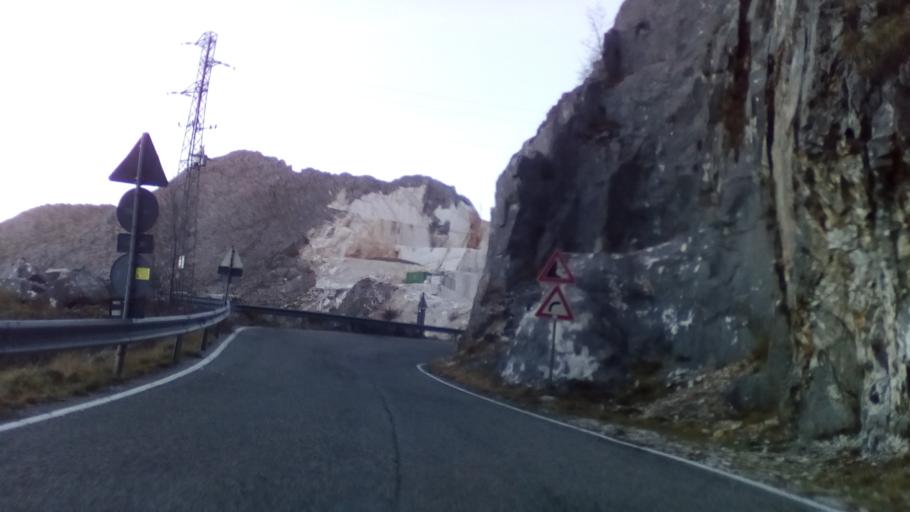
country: IT
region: Tuscany
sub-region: Provincia di Massa-Carrara
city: Montignoso
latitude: 44.0645
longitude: 10.2251
